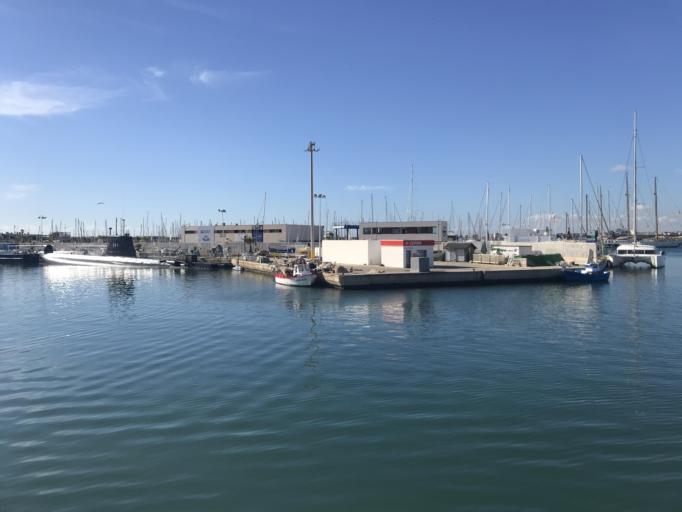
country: ES
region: Valencia
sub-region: Provincia de Alicante
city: Torrevieja
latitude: 37.9736
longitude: -0.6813
